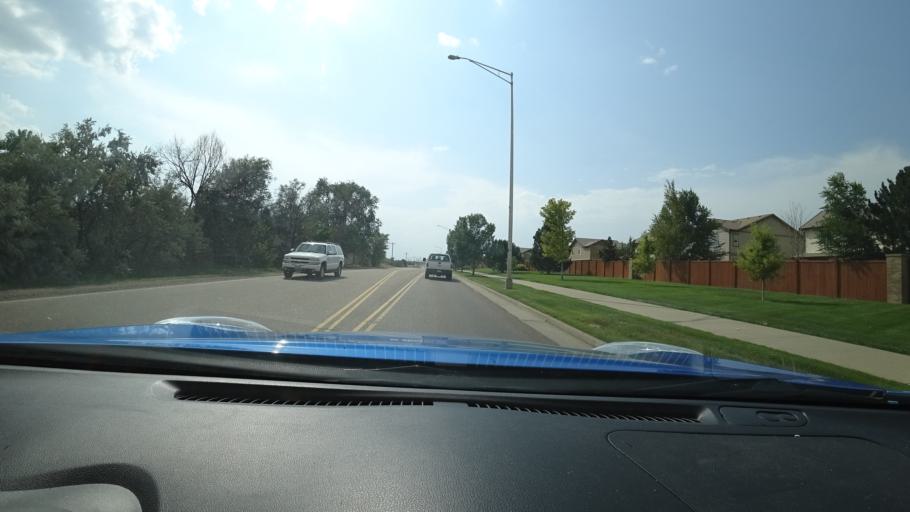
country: US
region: Colorado
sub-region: Adams County
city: Todd Creek
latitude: 39.9288
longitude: -104.8971
